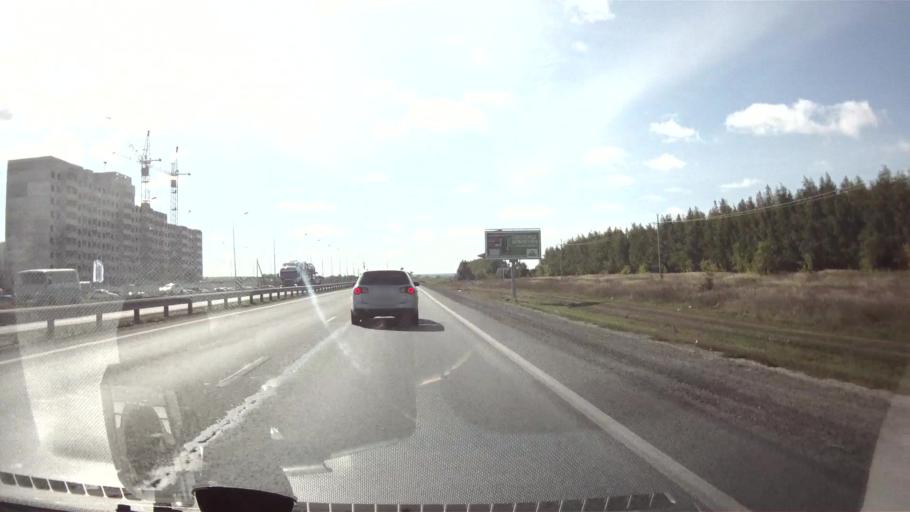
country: RU
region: Ulyanovsk
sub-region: Ulyanovskiy Rayon
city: Ulyanovsk
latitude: 54.2834
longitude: 48.2577
